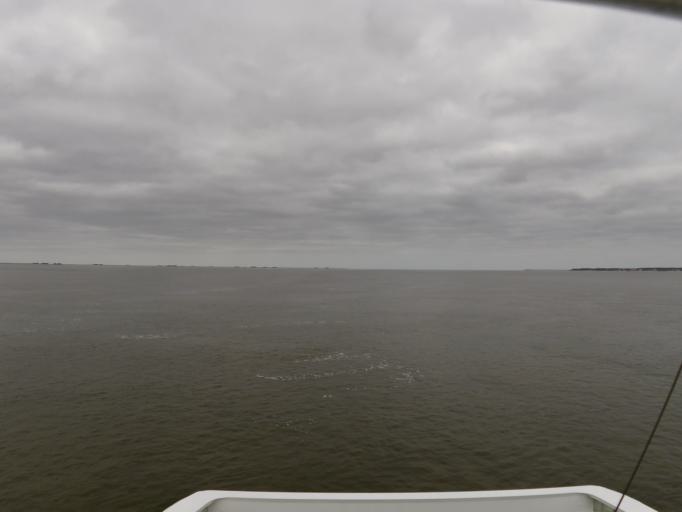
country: DE
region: Schleswig-Holstein
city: Wyk auf Fohr
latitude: 54.6973
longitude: 8.6338
